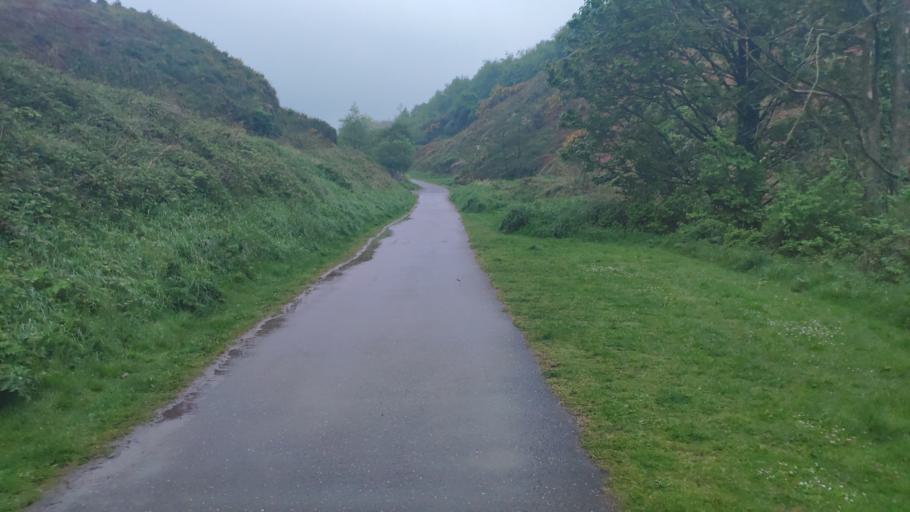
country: IE
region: Munster
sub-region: County Cork
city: Cork
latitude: 51.9139
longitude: -8.4628
